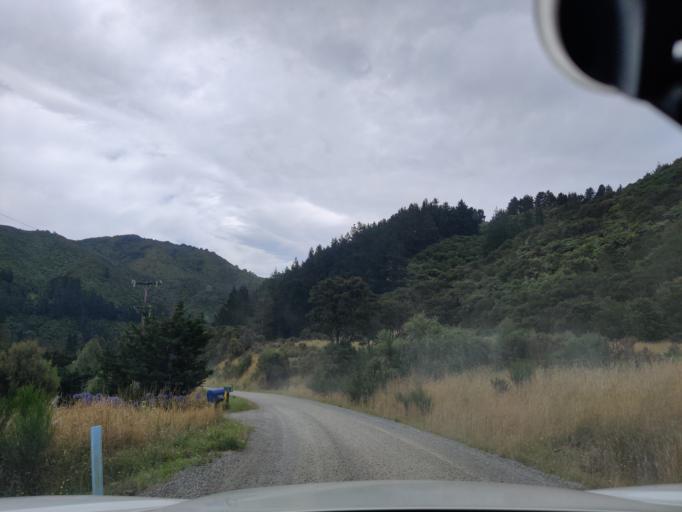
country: NZ
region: Wellington
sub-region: Masterton District
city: Masterton
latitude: -41.0356
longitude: 175.4001
